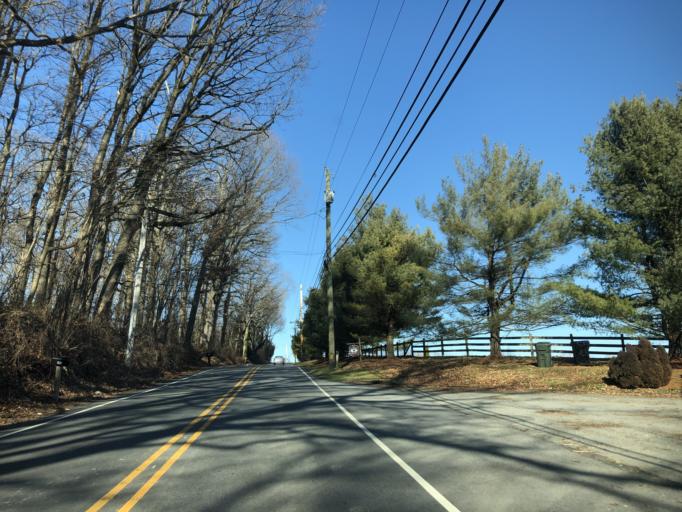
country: US
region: Pennsylvania
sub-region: Chester County
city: South Coatesville
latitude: 39.9429
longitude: -75.8342
